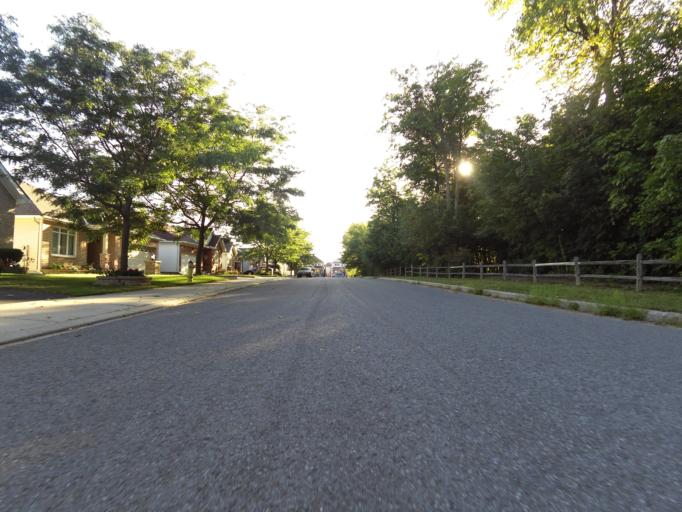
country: CA
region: Ontario
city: Bells Corners
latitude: 45.2810
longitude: -75.7243
